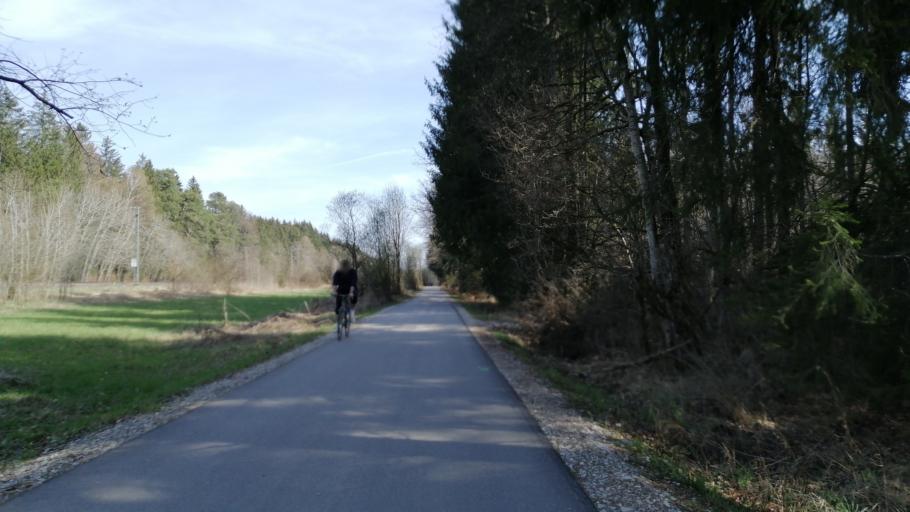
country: DE
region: Bavaria
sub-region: Upper Bavaria
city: Oberhaching
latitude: 47.9957
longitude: 11.6155
